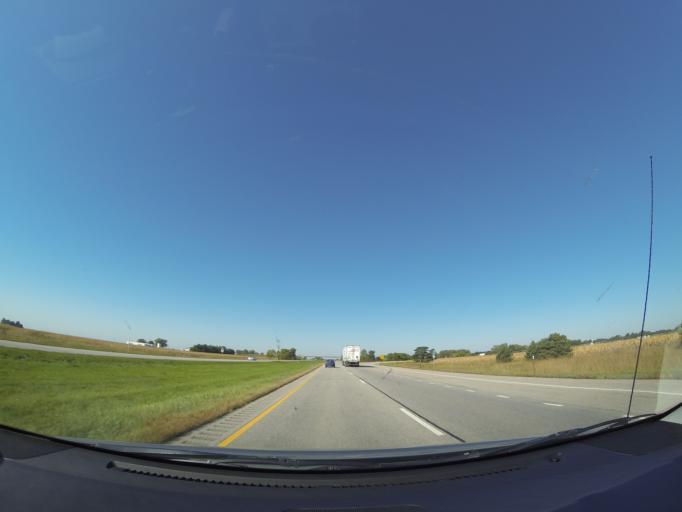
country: US
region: Nebraska
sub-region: Seward County
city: Seward
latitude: 40.8226
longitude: -97.2101
